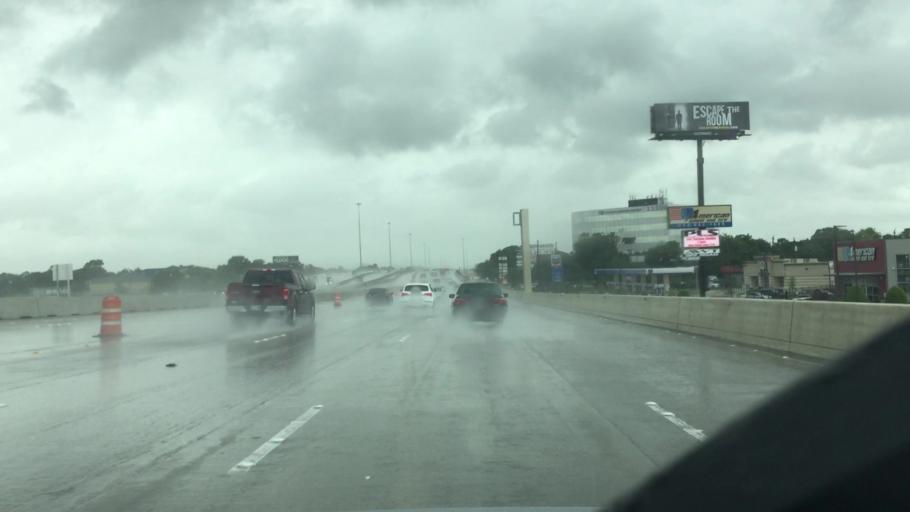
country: US
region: Texas
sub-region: Harris County
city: Spring Valley
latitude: 29.8206
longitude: -95.4696
